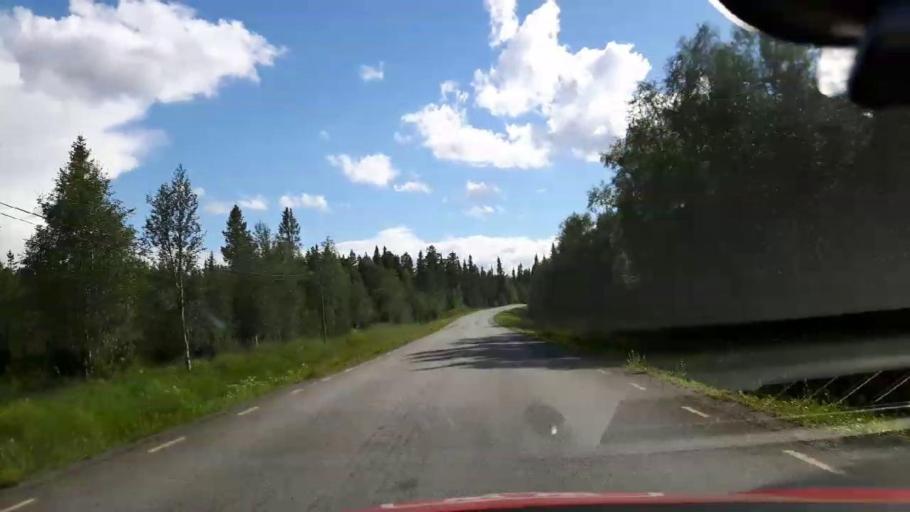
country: SE
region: Jaemtland
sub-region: Are Kommun
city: Are
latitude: 63.2180
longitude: 13.1643
